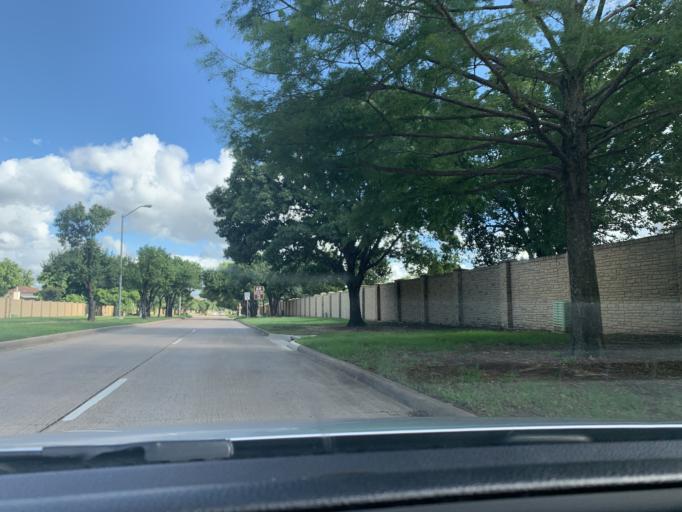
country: US
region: Texas
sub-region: Dallas County
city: Grand Prairie
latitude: 32.6674
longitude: -97.0436
